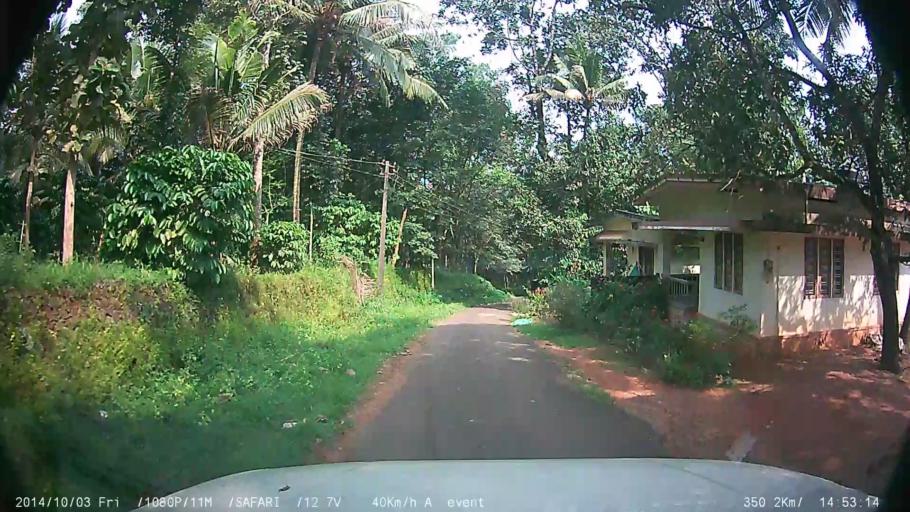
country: IN
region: Kerala
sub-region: Kottayam
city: Palackattumala
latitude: 9.7882
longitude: 76.5699
